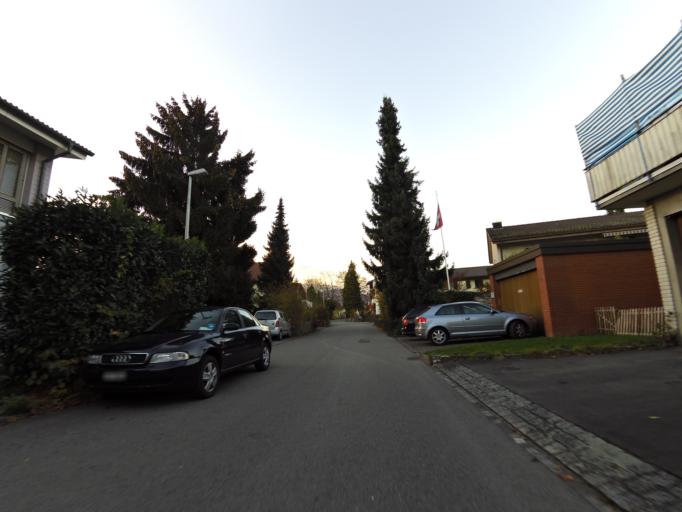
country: CH
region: Aargau
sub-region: Bezirk Aarau
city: Buchs
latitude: 47.3874
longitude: 8.0725
